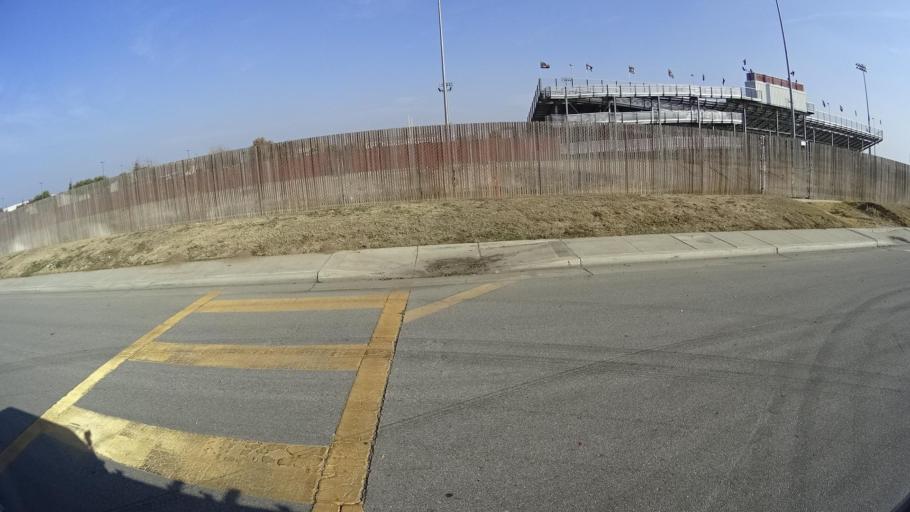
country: US
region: California
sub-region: Kern County
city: Delano
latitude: 35.7651
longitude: -119.2232
